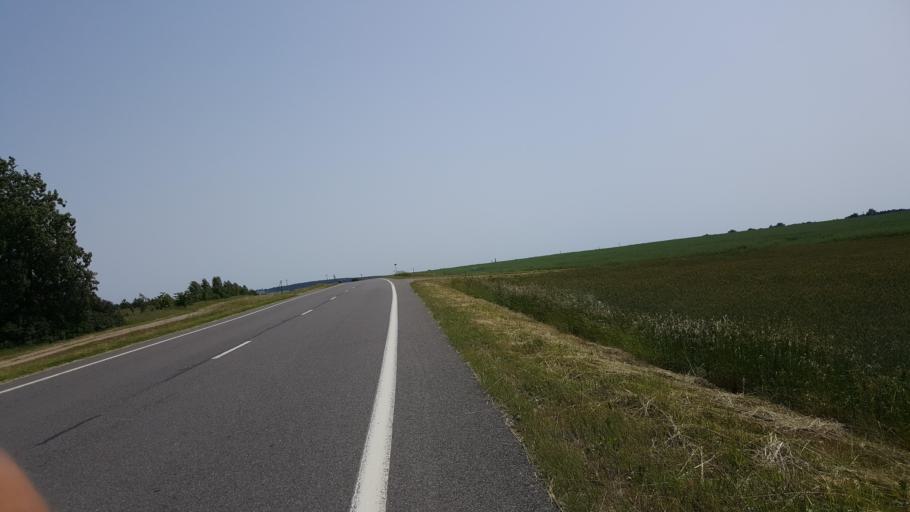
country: BY
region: Brest
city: Kamyanyets
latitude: 52.4373
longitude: 23.8314
